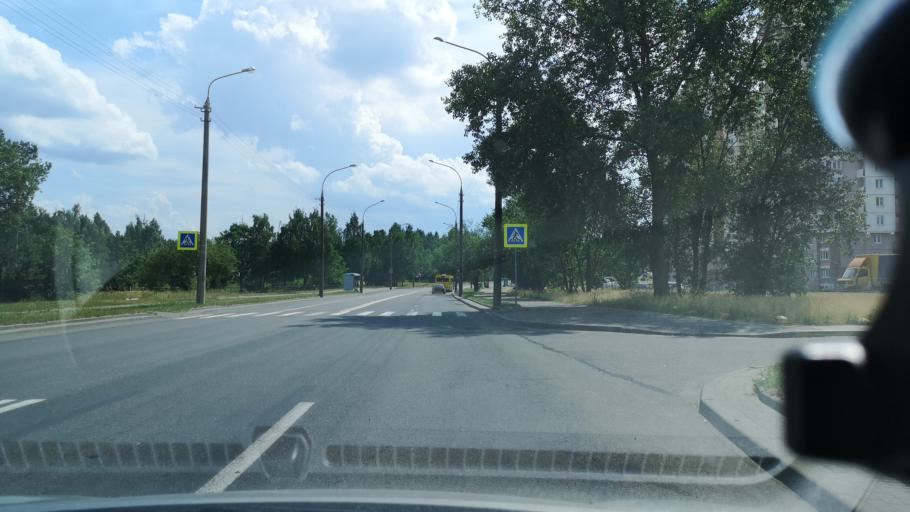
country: BY
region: Minsk
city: Lyeskawka
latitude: 53.9308
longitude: 27.6998
